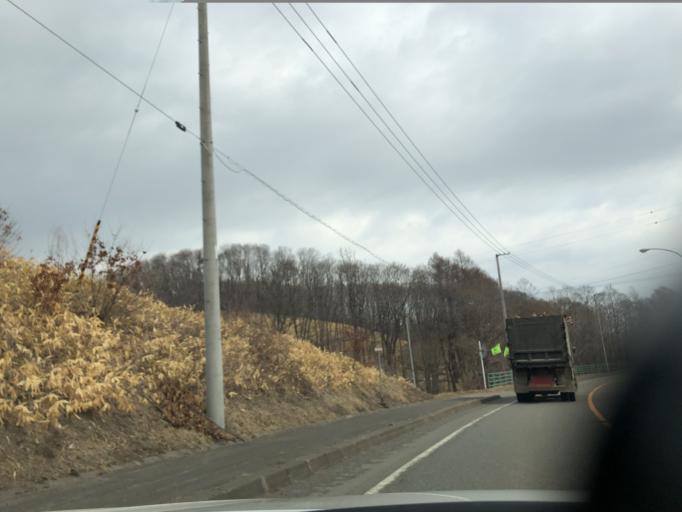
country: JP
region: Hokkaido
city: Chitose
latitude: 42.7632
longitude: 141.8039
